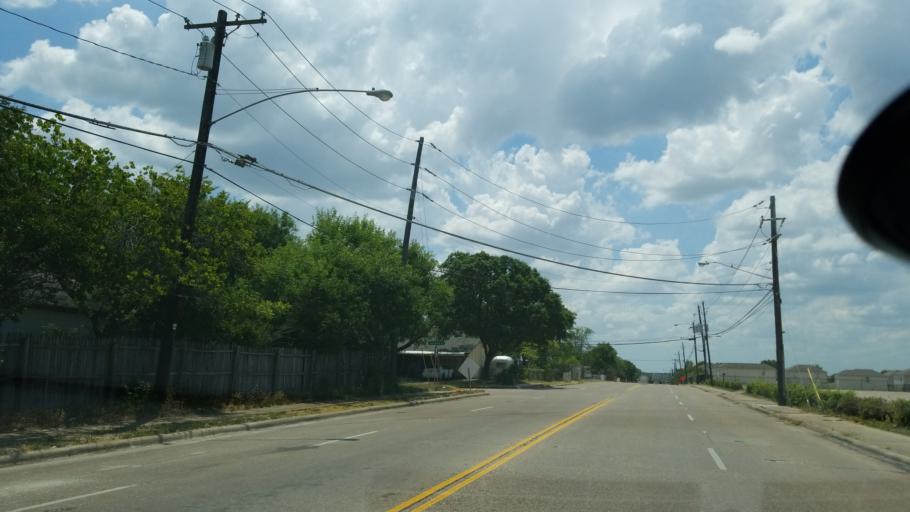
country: US
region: Texas
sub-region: Dallas County
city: Cockrell Hill
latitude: 32.7203
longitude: -96.9001
